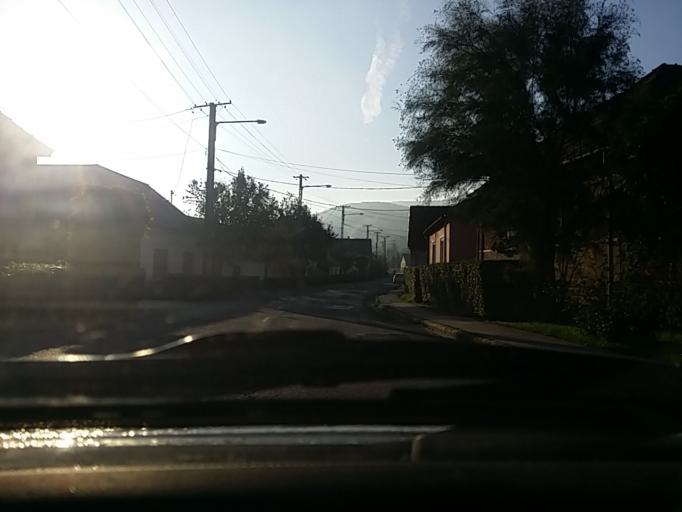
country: HU
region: Komarom-Esztergom
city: Pilismarot
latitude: 47.7668
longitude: 18.9051
